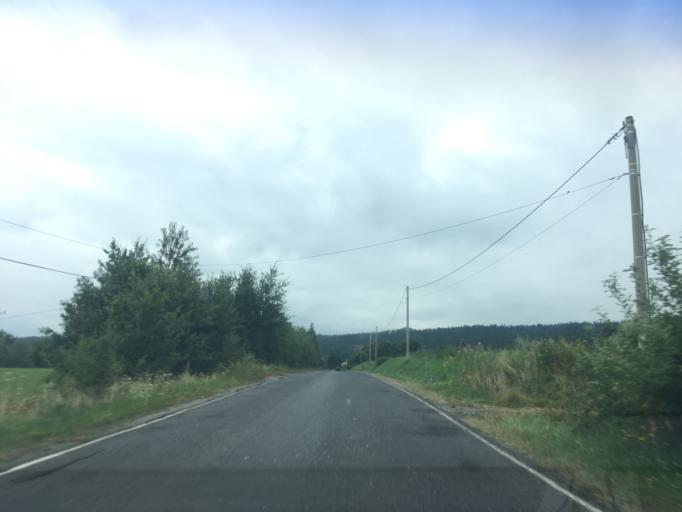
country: PL
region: Lesser Poland Voivodeship
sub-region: Powiat myslenicki
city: Dobczyce
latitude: 49.8439
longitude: 20.0752
